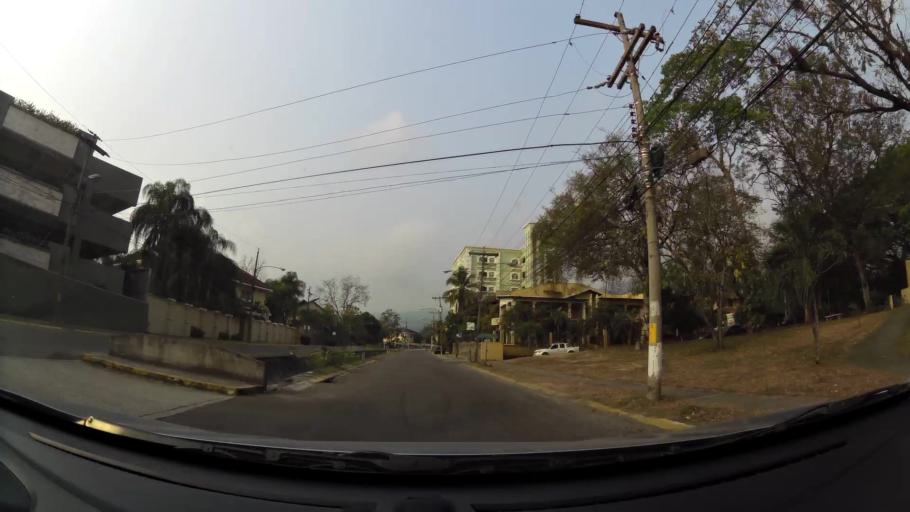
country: HN
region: Cortes
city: Armenta
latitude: 15.4914
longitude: -88.0374
